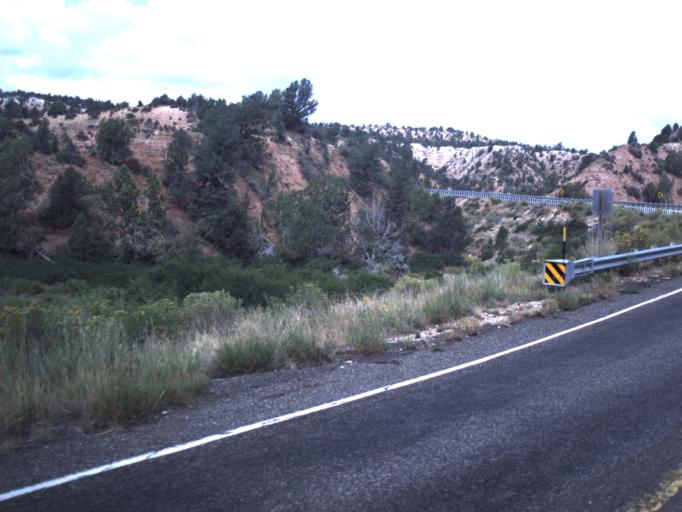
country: US
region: Utah
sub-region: Kane County
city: Kanab
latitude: 37.2268
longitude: -112.6845
